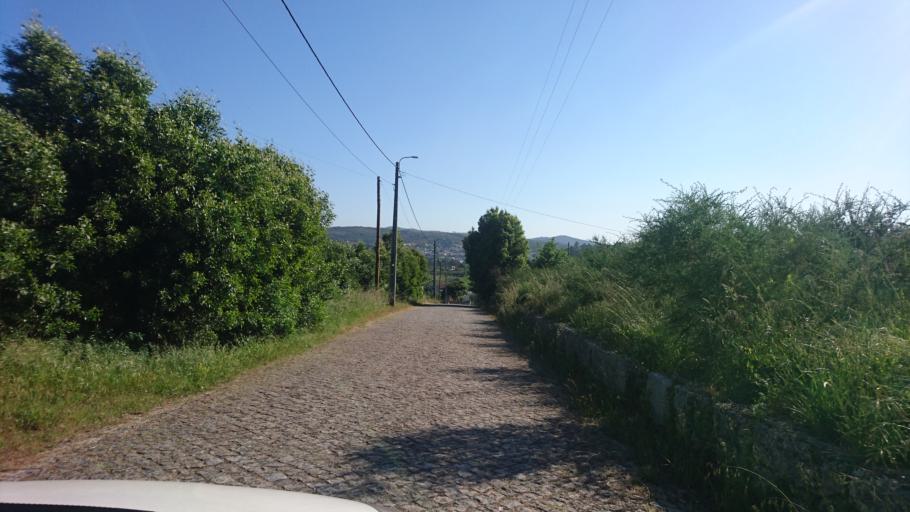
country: PT
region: Porto
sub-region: Paredes
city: Baltar
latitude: 41.1600
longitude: -8.3788
